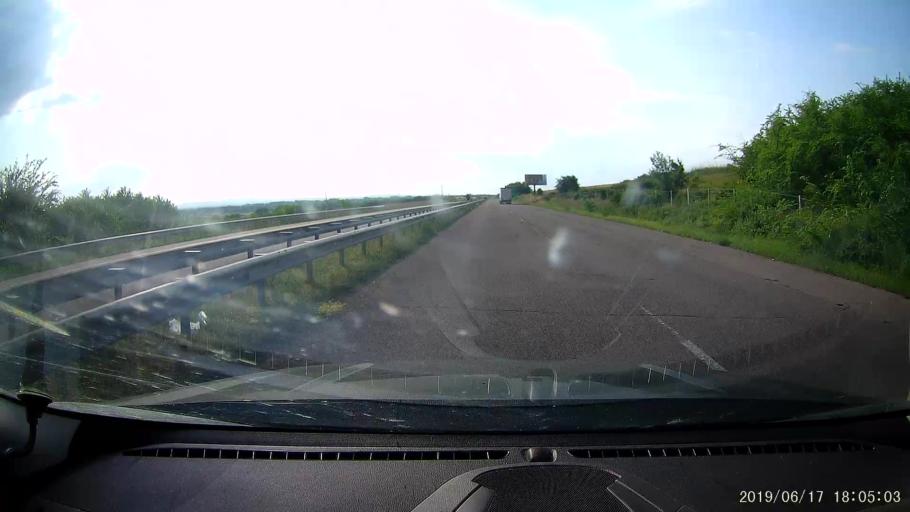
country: BG
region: Khaskovo
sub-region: Obshtina Svilengrad
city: Svilengrad
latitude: 41.7933
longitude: 26.1846
